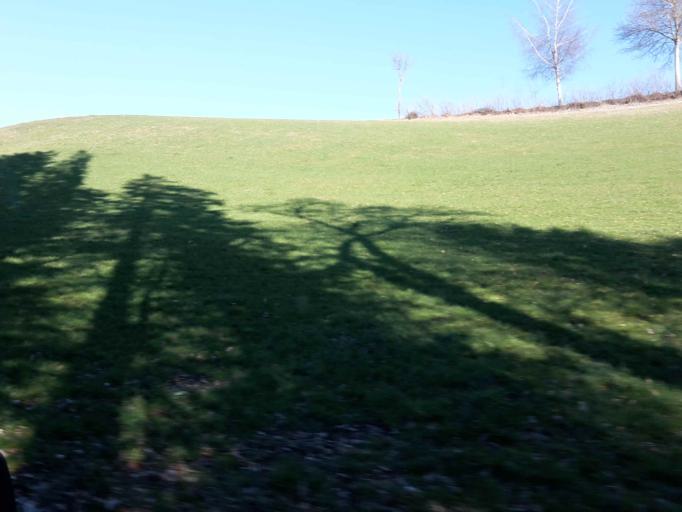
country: CH
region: Bern
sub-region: Emmental District
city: Durrenroth
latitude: 47.1167
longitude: 7.7884
